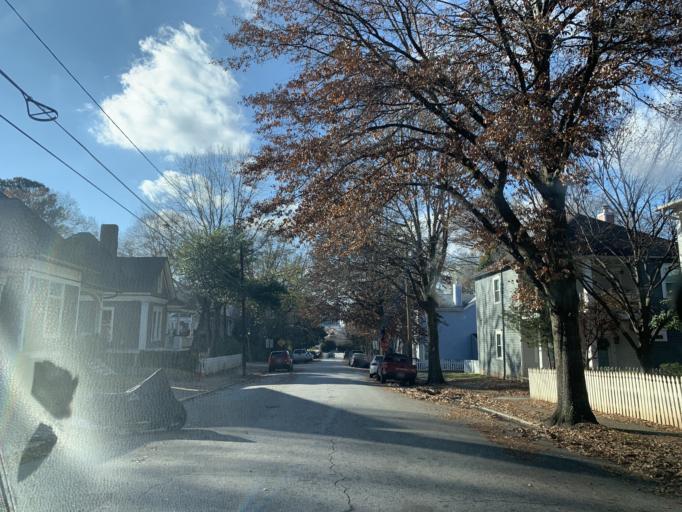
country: US
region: Georgia
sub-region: Fulton County
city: Atlanta
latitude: 33.7425
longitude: -84.3774
